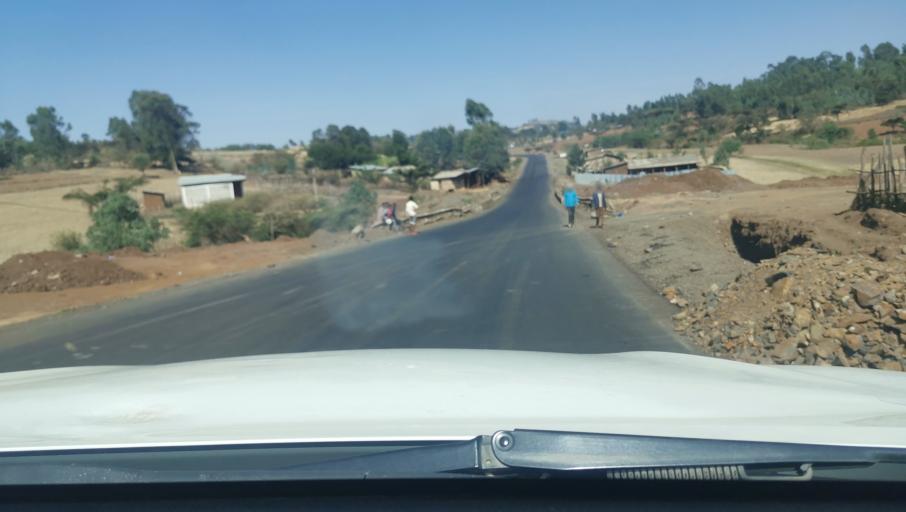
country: ET
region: Oromiya
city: Gedo
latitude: 8.9657
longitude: 37.5305
